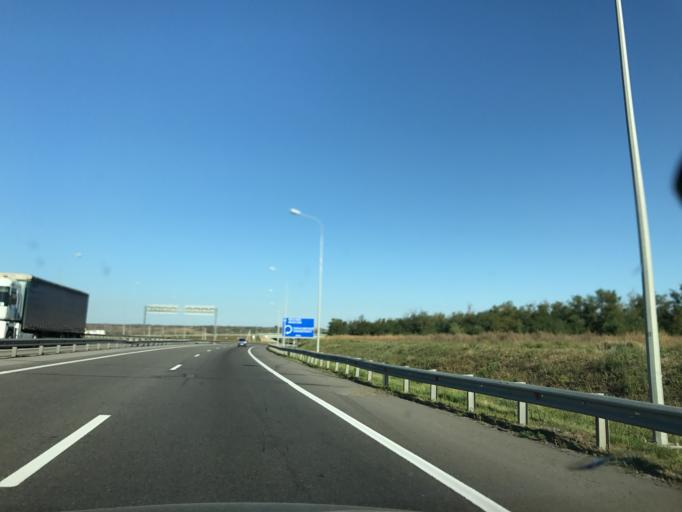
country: RU
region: Rostov
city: Tarasovskiy
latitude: 48.7497
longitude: 40.3794
